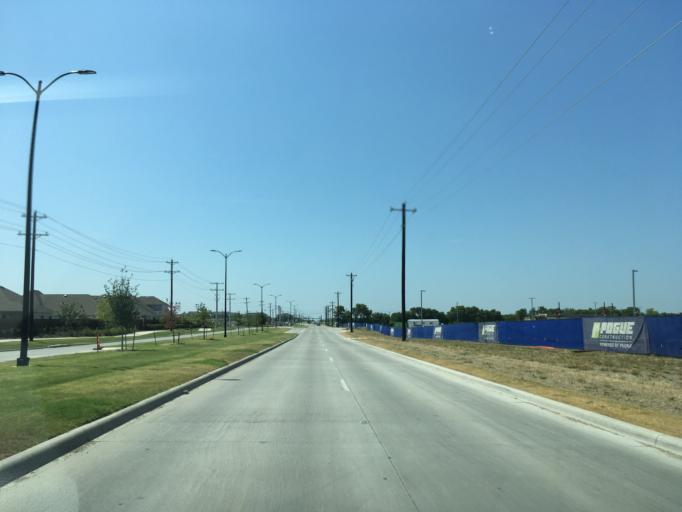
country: US
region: Texas
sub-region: Collin County
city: Prosper
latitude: 33.2091
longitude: -96.7677
